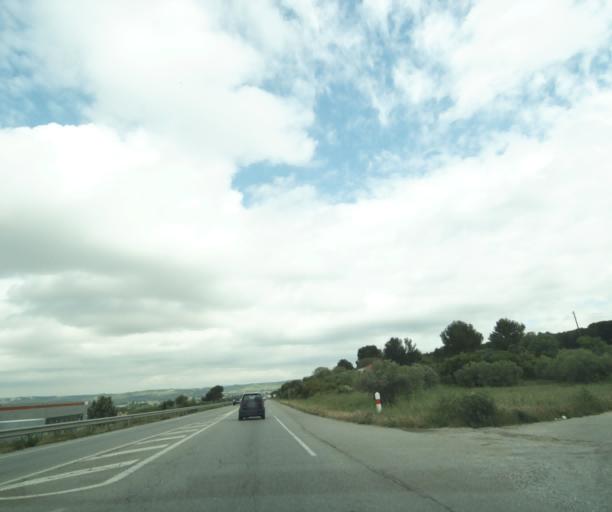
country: FR
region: Provence-Alpes-Cote d'Azur
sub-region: Departement des Bouches-du-Rhone
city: La Fare-les-Oliviers
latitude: 43.5209
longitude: 5.1989
